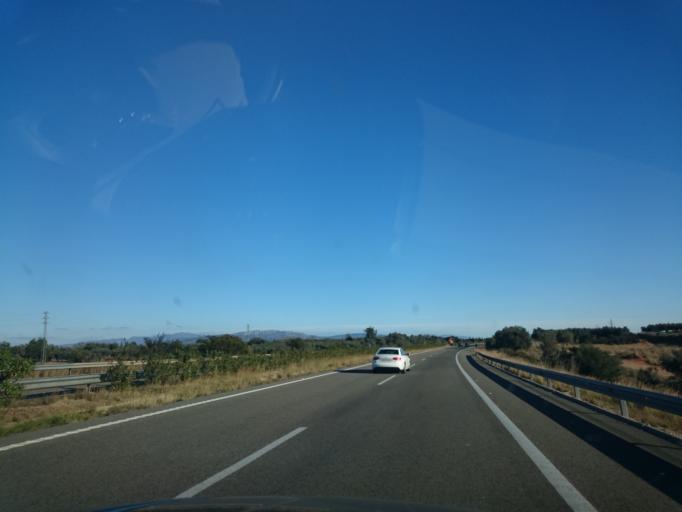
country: ES
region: Catalonia
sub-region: Provincia de Tarragona
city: Masdenverge
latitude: 40.6911
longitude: 0.5302
